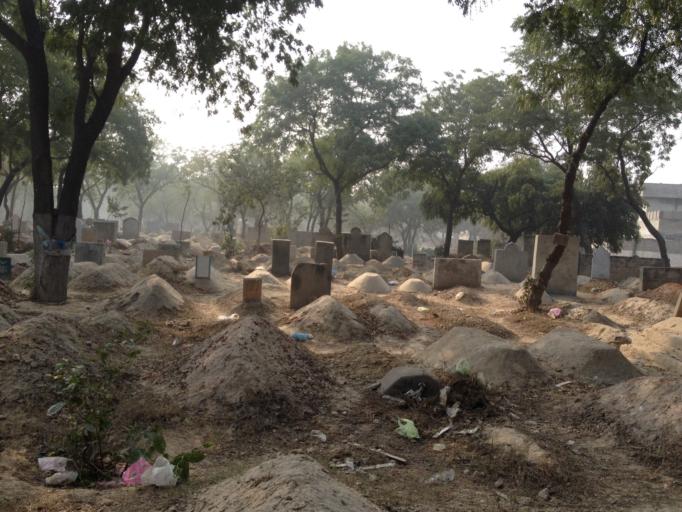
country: PK
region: Punjab
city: Lahore
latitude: 31.5777
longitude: 74.4155
